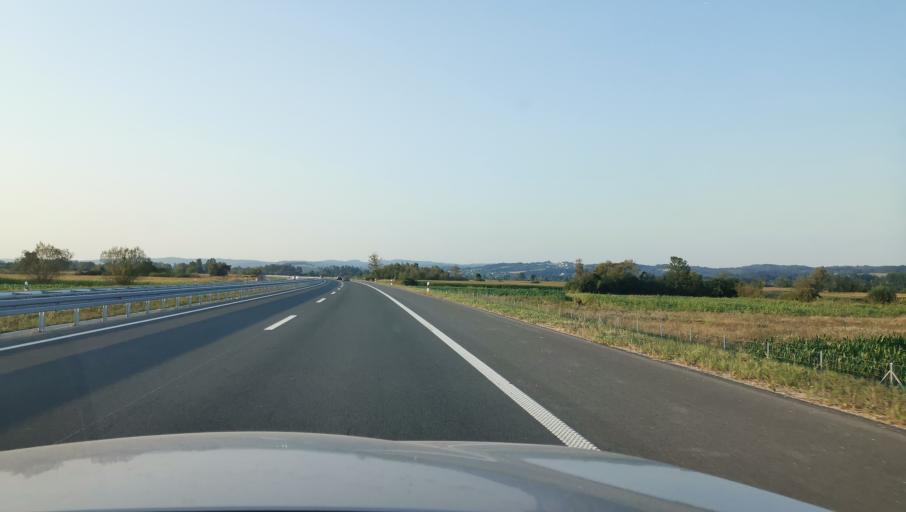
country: RS
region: Central Serbia
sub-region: Kolubarski Okrug
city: Ljig
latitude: 44.2543
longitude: 20.2704
